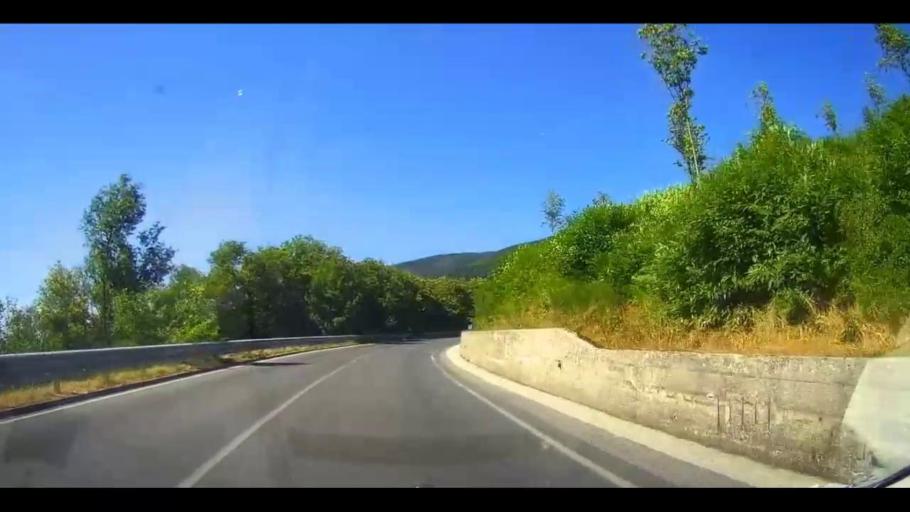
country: IT
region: Calabria
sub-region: Provincia di Cosenza
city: Celico
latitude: 39.3117
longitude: 16.3547
